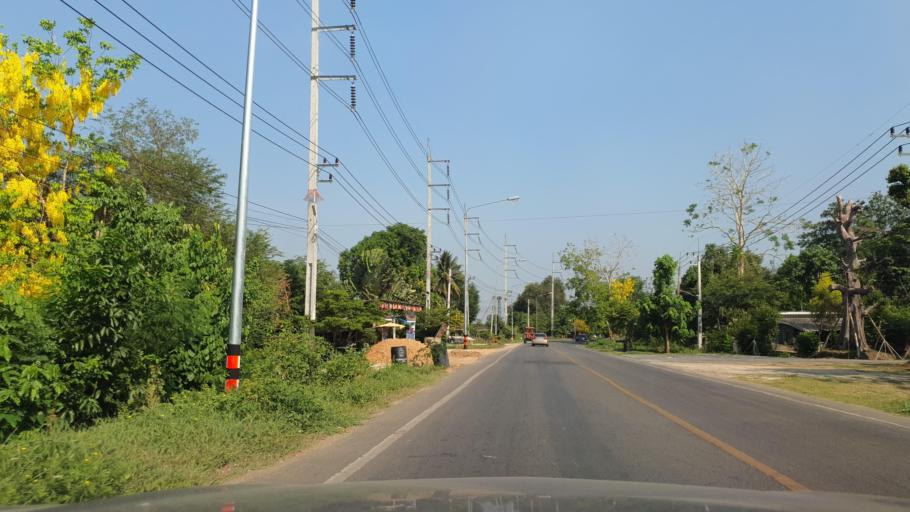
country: TH
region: Kanchanaburi
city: Kanchanaburi
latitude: 14.0395
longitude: 99.4754
